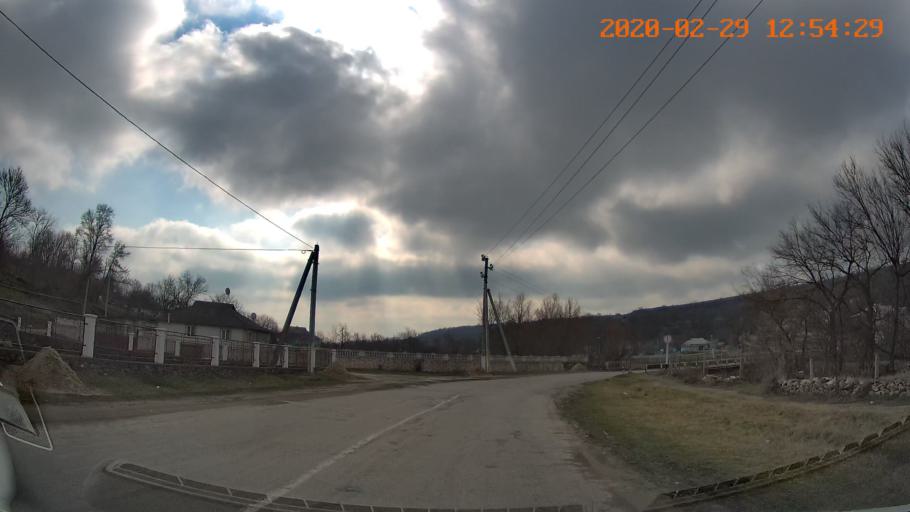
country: MD
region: Telenesti
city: Camenca
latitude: 48.1014
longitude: 28.7274
